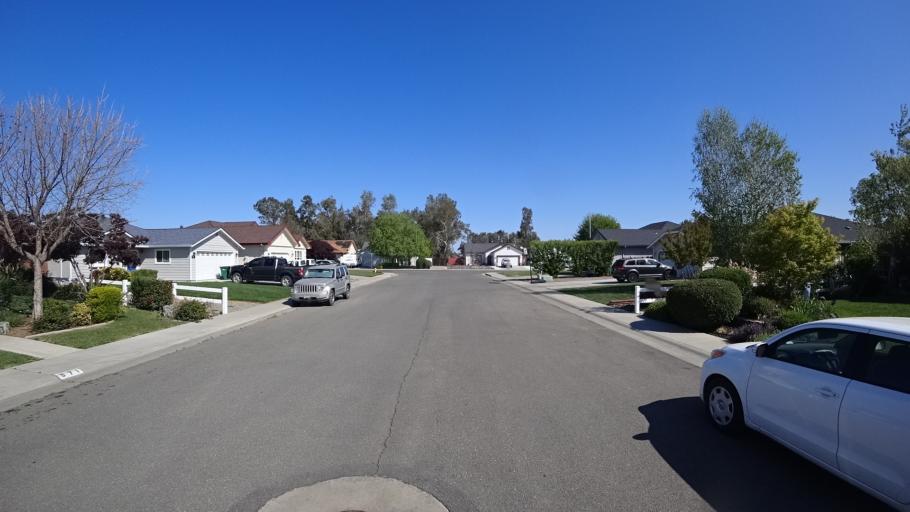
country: US
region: California
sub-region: Glenn County
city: Willows
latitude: 39.5304
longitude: -122.2055
